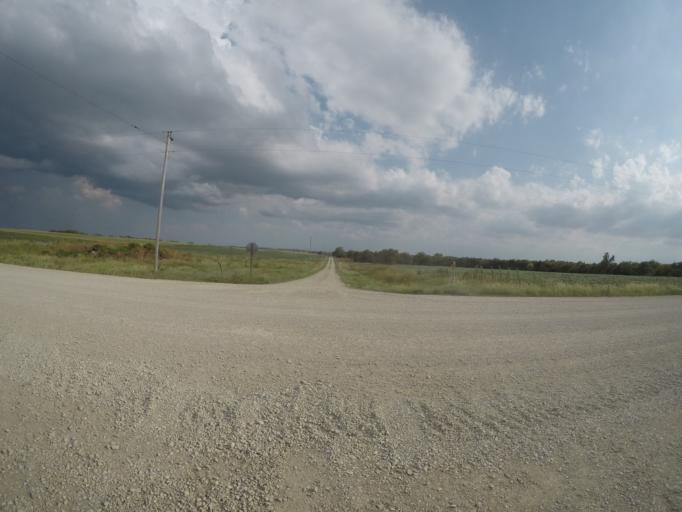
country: US
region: Kansas
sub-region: Marshall County
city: Blue Rapids
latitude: 39.5377
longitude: -96.8291
